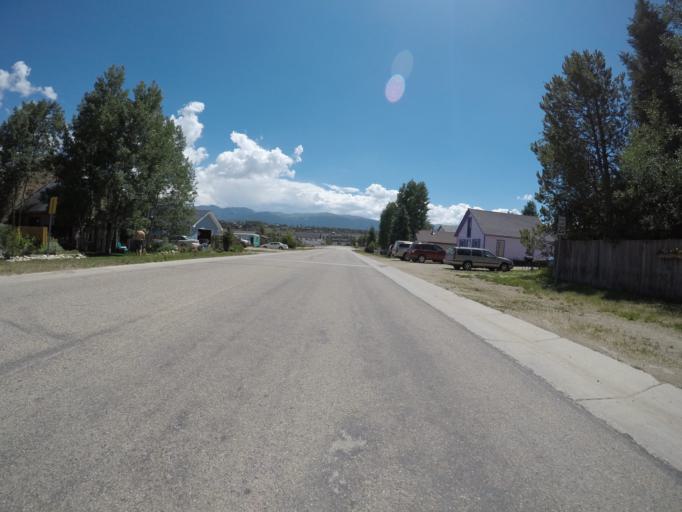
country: US
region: Colorado
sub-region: Grand County
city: Fraser
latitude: 39.9467
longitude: -105.8191
